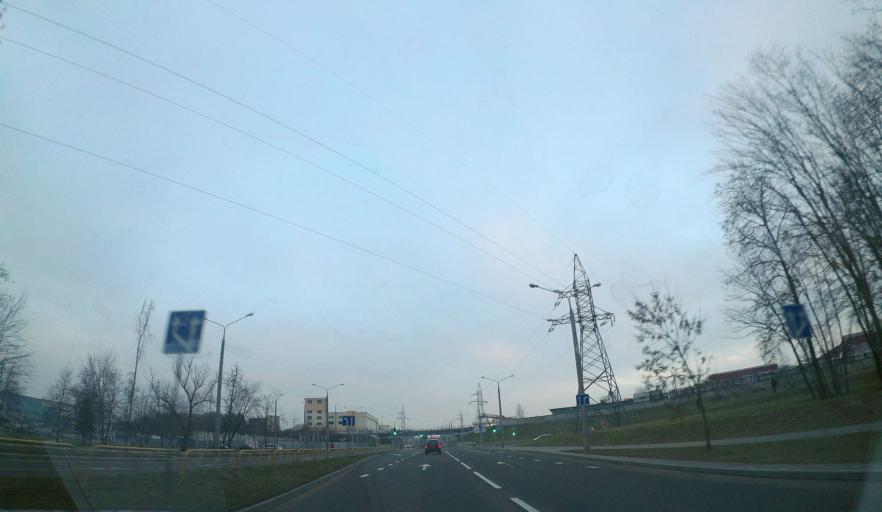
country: BY
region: Grodnenskaya
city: Hrodna
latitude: 53.6553
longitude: 23.7857
